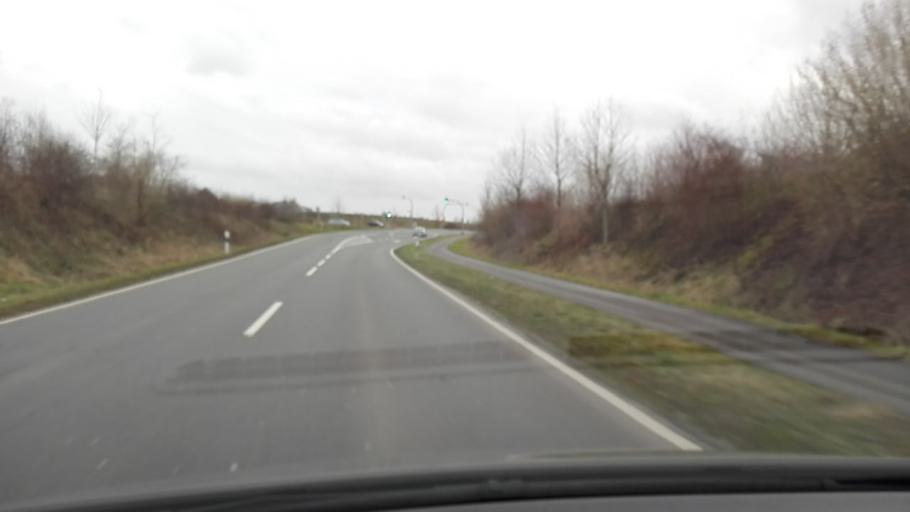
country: DE
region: North Rhine-Westphalia
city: Lanstrop
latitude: 51.5250
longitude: 7.5772
